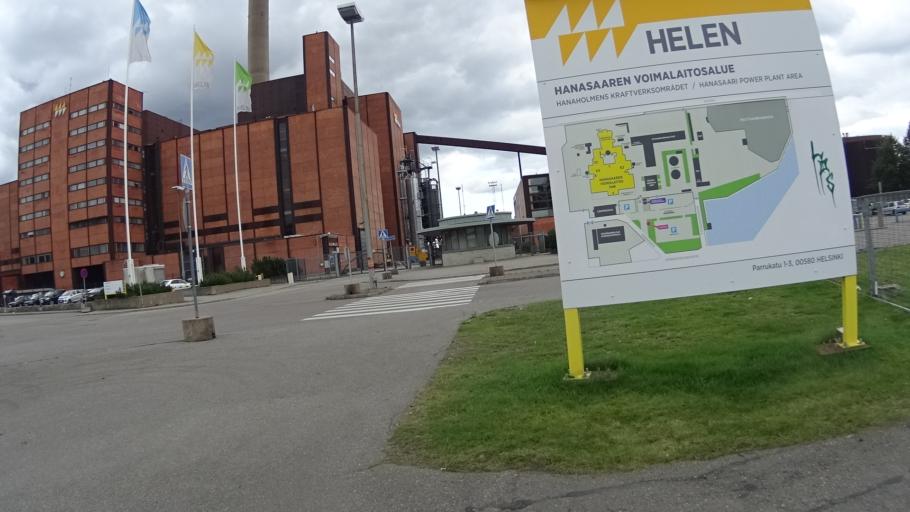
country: FI
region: Uusimaa
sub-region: Helsinki
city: Helsinki
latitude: 60.1843
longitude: 24.9680
